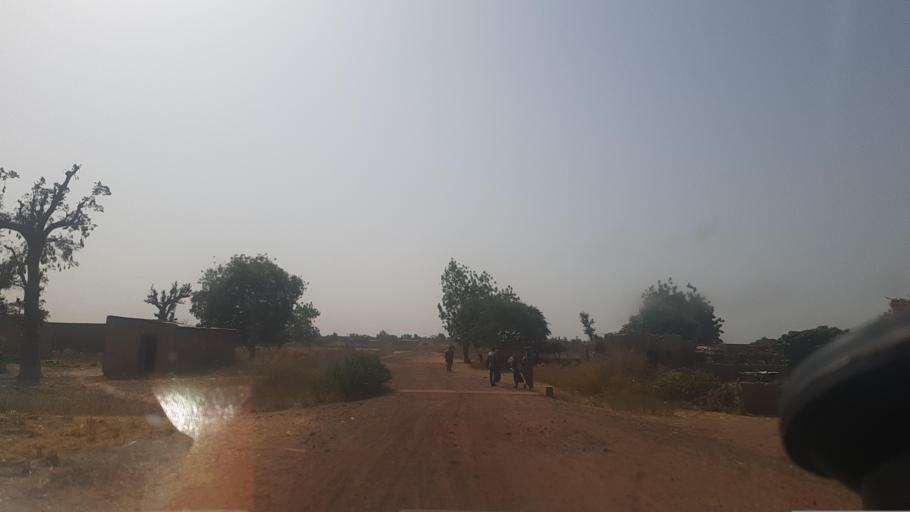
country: ML
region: Segou
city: Baroueli
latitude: 13.1645
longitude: -6.5182
